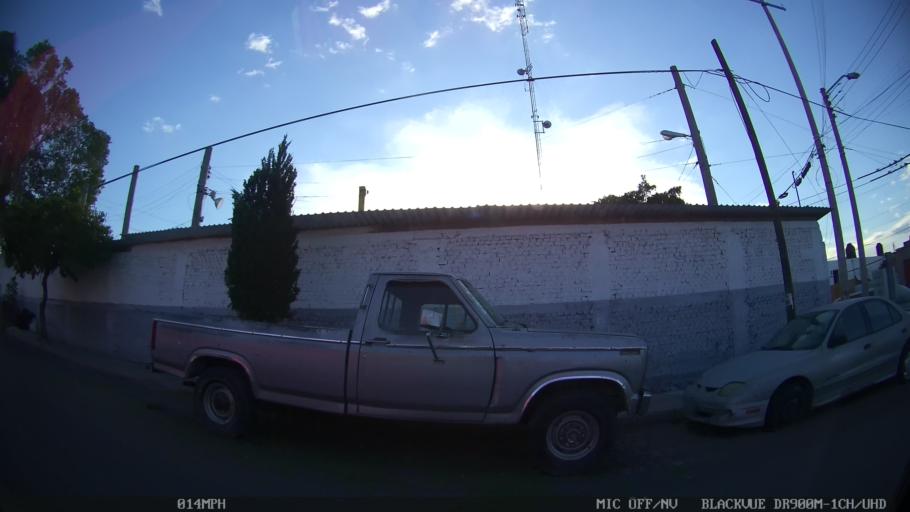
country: MX
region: Jalisco
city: Tlaquepaque
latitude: 20.7082
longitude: -103.3022
